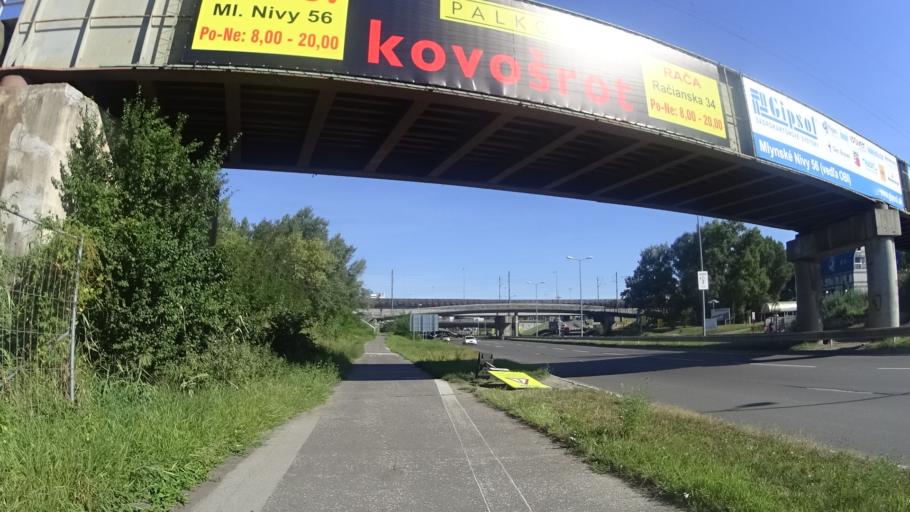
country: SK
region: Bratislavsky
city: Bratislava
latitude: 48.1391
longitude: 17.1523
